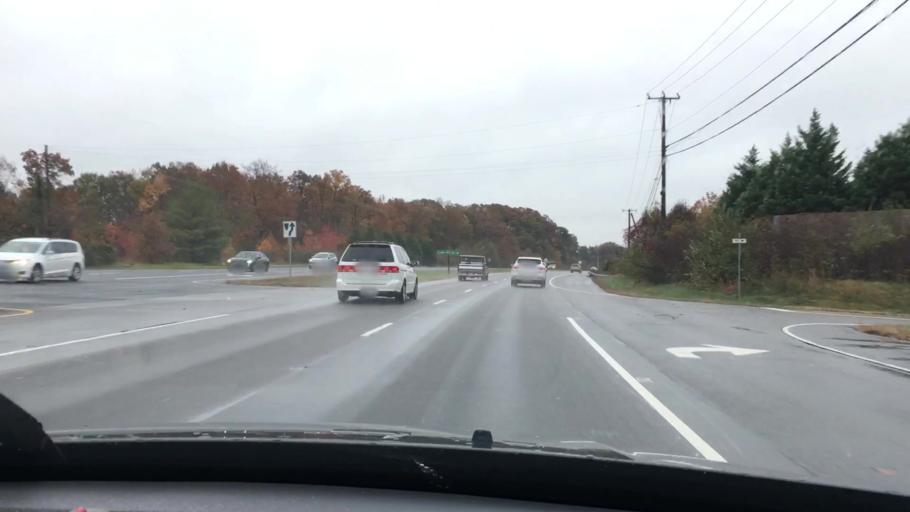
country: US
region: Virginia
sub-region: Prince William County
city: Lake Ridge
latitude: 38.7193
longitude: -77.2742
